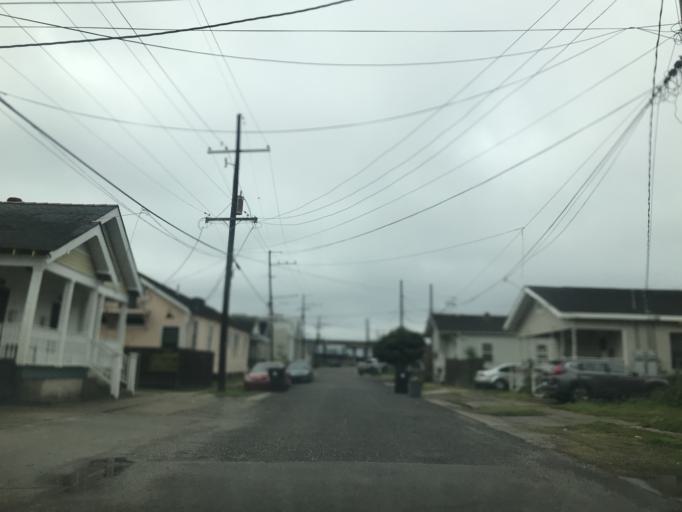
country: US
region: Louisiana
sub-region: Orleans Parish
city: New Orleans
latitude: 29.9736
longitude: -90.1085
